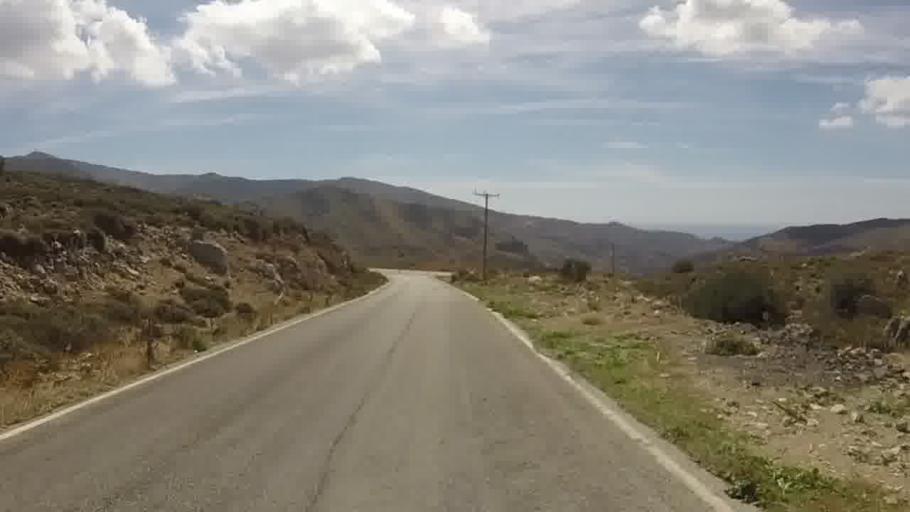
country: GR
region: Crete
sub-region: Nomos Rethymnis
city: Agia Galini
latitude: 35.1523
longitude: 24.6213
